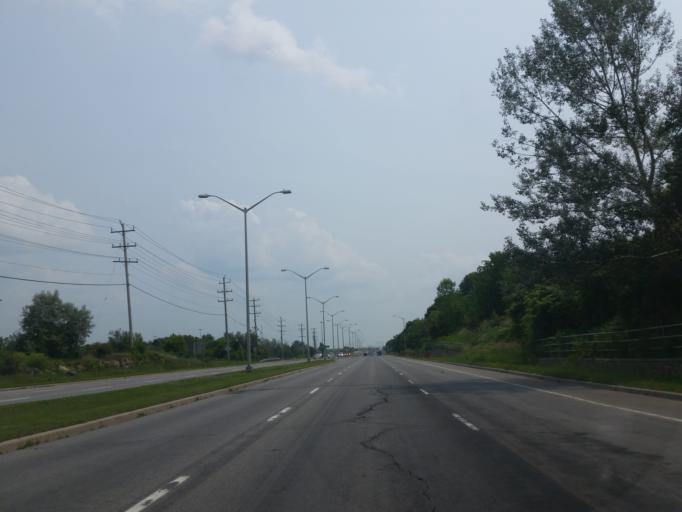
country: CA
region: Ontario
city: Bells Corners
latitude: 45.3282
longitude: -75.8907
